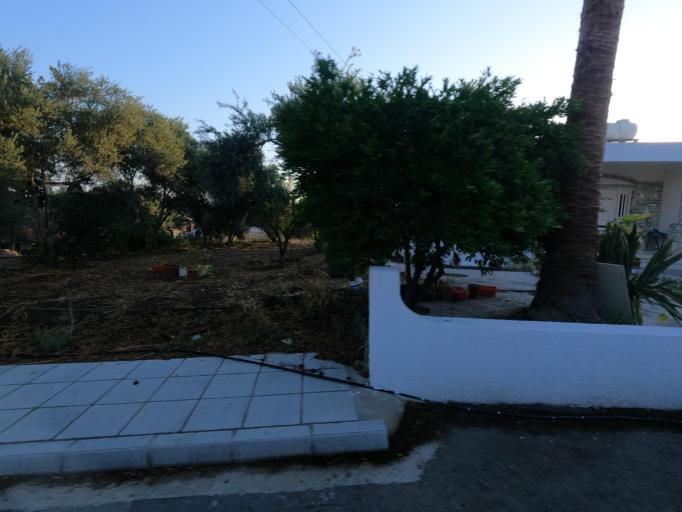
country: CY
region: Lefkosia
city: Alampra
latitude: 34.9877
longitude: 33.4019
